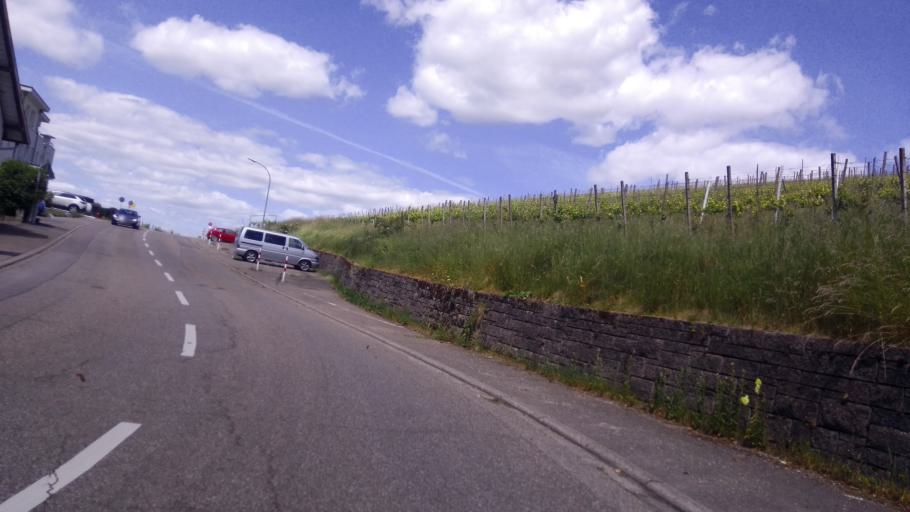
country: DE
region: Baden-Wuerttemberg
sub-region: Karlsruhe Region
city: Sinzheim
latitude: 48.7303
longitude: 8.1776
